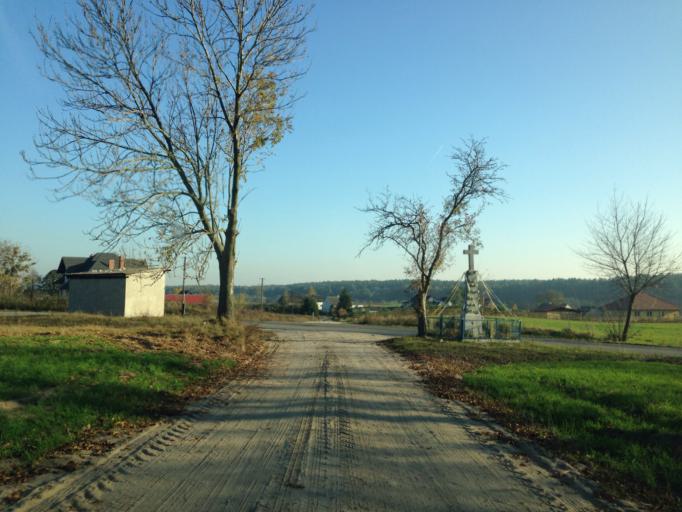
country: PL
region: Kujawsko-Pomorskie
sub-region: Powiat brodnicki
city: Gorzno
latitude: 53.1693
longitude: 19.6177
